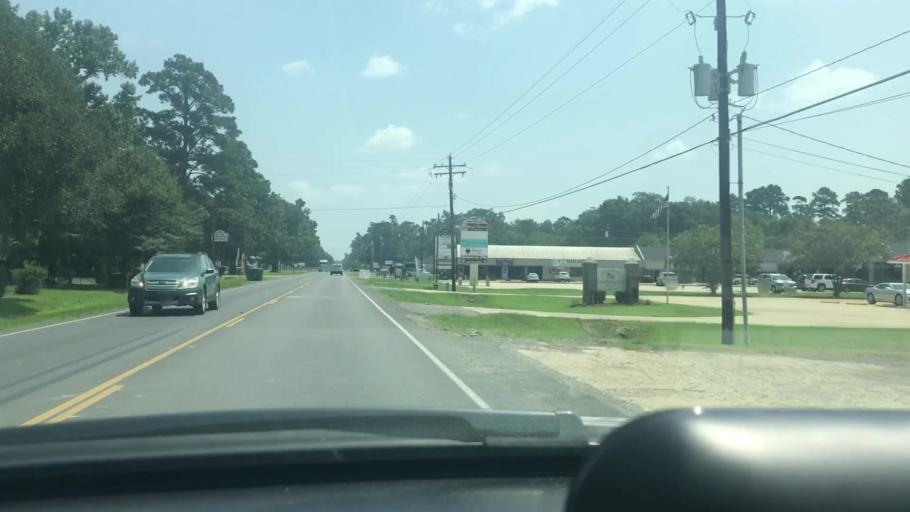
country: US
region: Louisiana
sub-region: Livingston Parish
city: Walker
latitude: 30.4854
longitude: -90.8885
